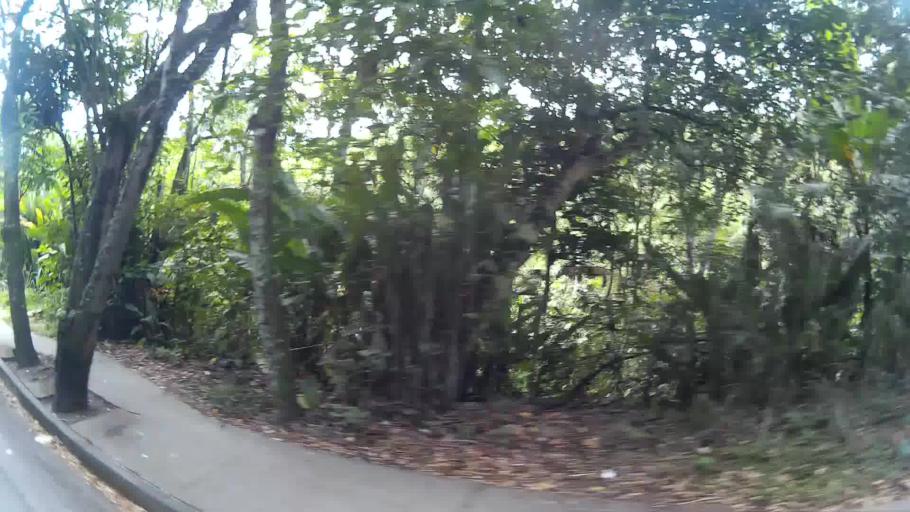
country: CO
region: Risaralda
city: Pereira
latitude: 4.8258
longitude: -75.7568
